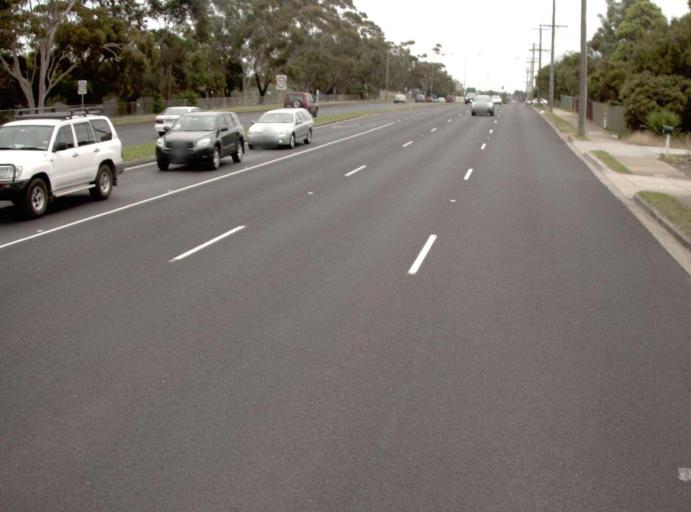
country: AU
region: Victoria
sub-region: Mornington Peninsula
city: Mornington
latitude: -38.2331
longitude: 145.0404
